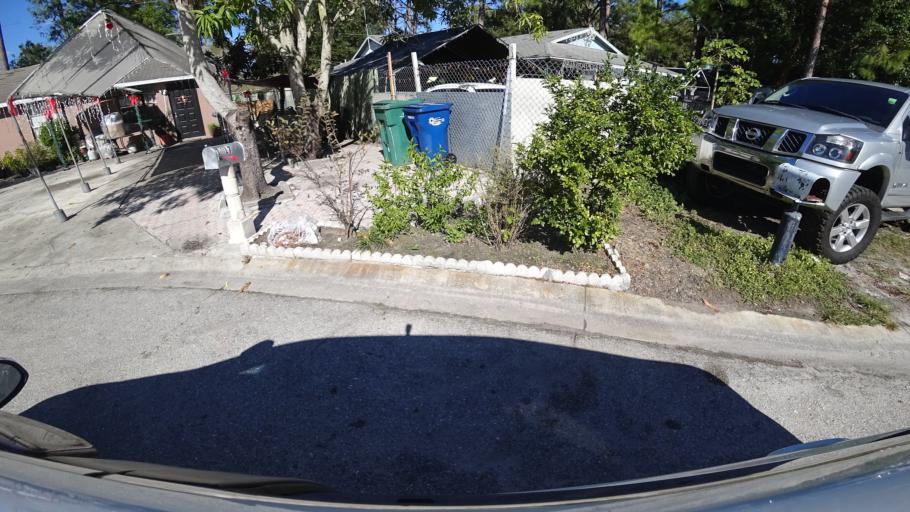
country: US
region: Florida
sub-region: Manatee County
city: Whitfield
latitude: 27.4301
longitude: -82.5516
